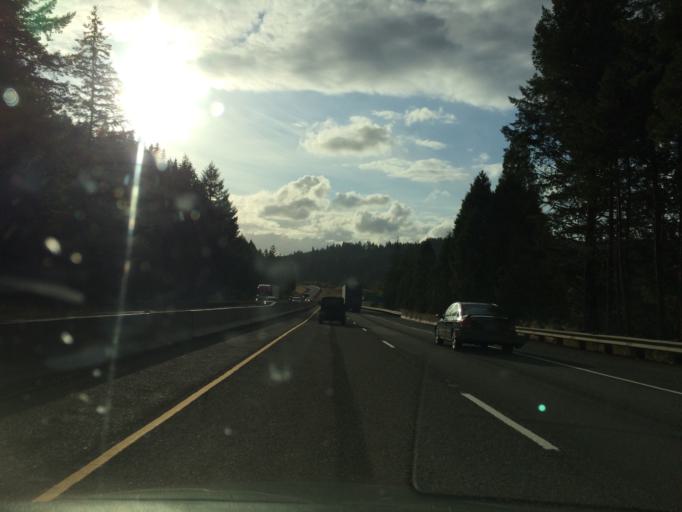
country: US
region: Oregon
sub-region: Douglas County
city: Drain
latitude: 43.7066
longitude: -123.2110
